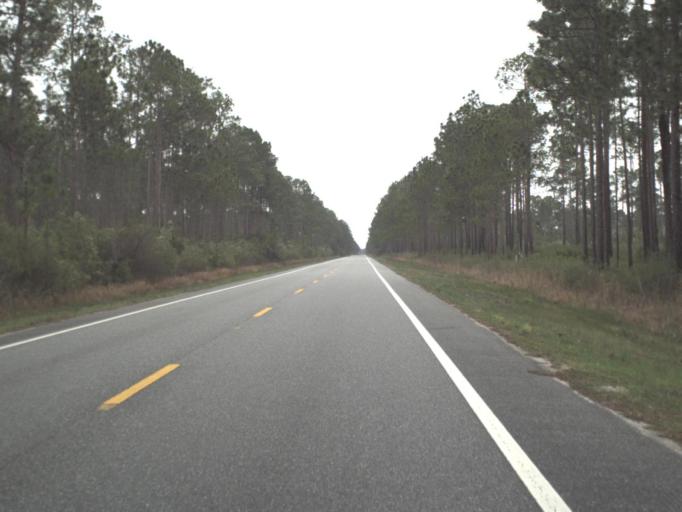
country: US
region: Florida
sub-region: Franklin County
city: Apalachicola
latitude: 29.8931
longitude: -84.9777
